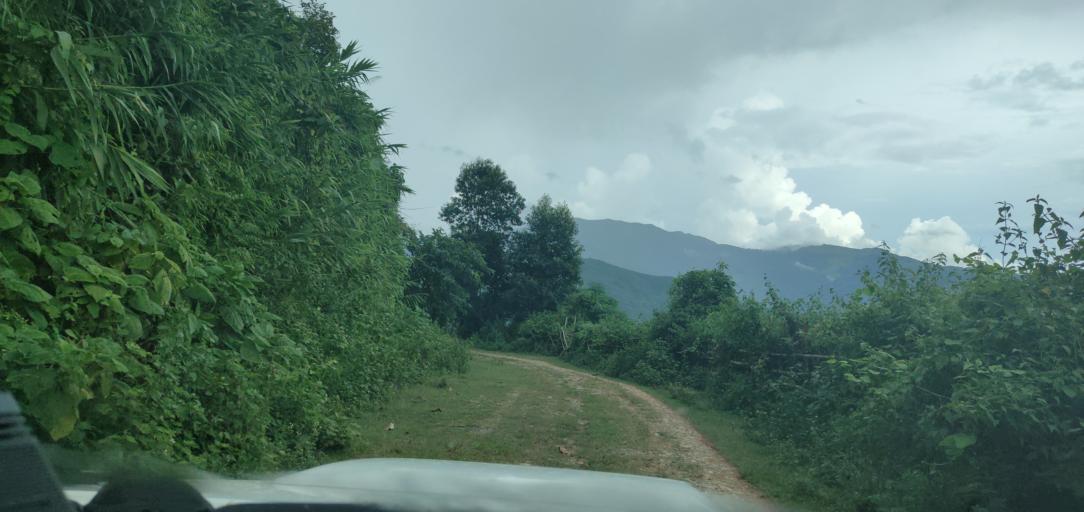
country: LA
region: Phongsali
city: Phongsali
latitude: 21.4416
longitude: 102.3268
